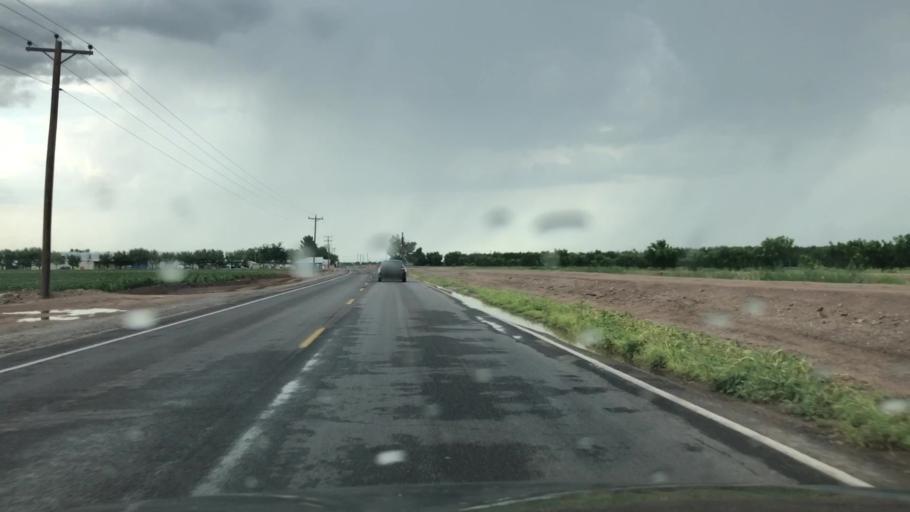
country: US
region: New Mexico
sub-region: Dona Ana County
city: Berino
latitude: 32.0568
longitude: -106.6759
